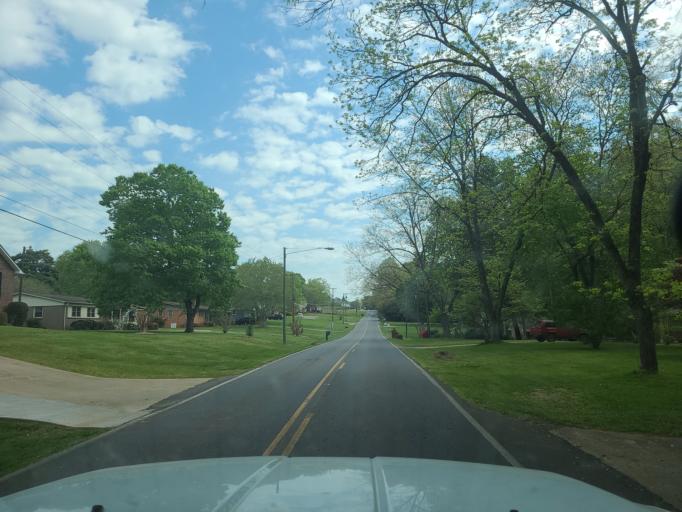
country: US
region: North Carolina
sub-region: Cleveland County
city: Shelby
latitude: 35.2884
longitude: -81.5055
